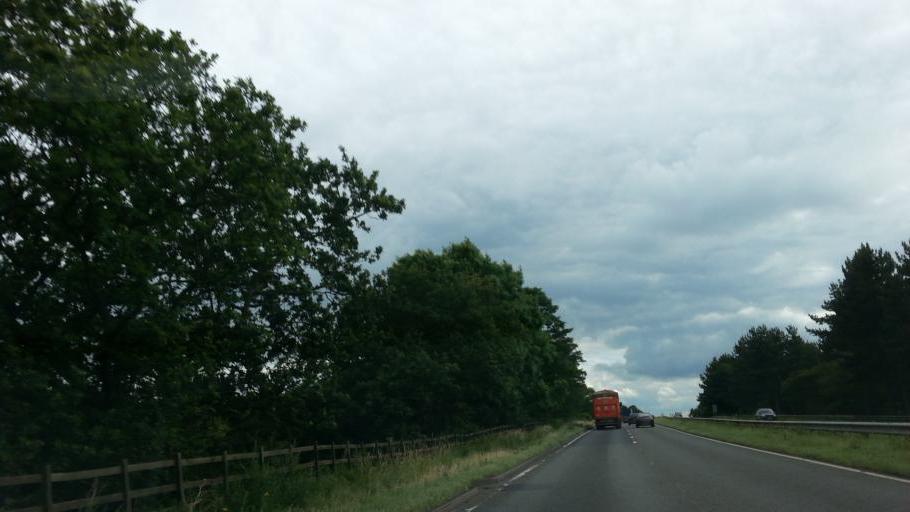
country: GB
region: England
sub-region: Nottinghamshire
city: Babworth
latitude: 53.3220
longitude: -1.0275
